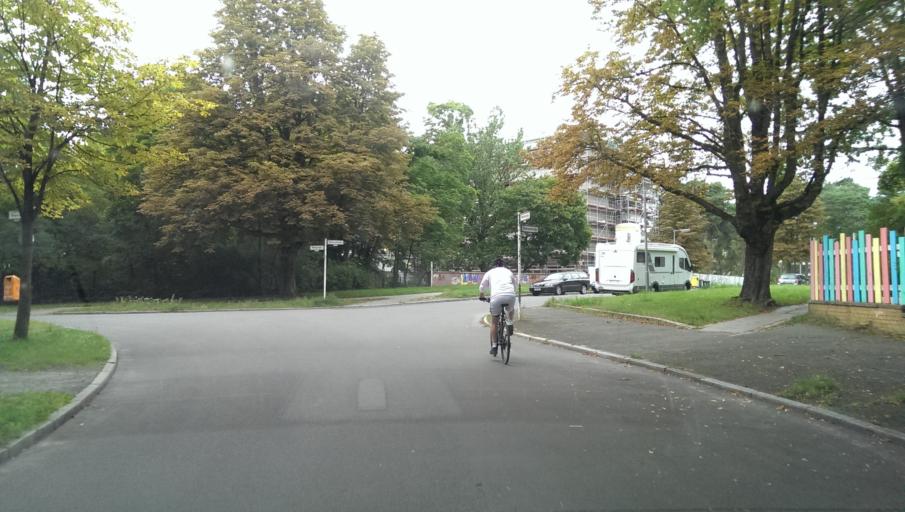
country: DE
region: Berlin
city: Zehlendorf Bezirk
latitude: 52.4503
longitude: 13.2627
